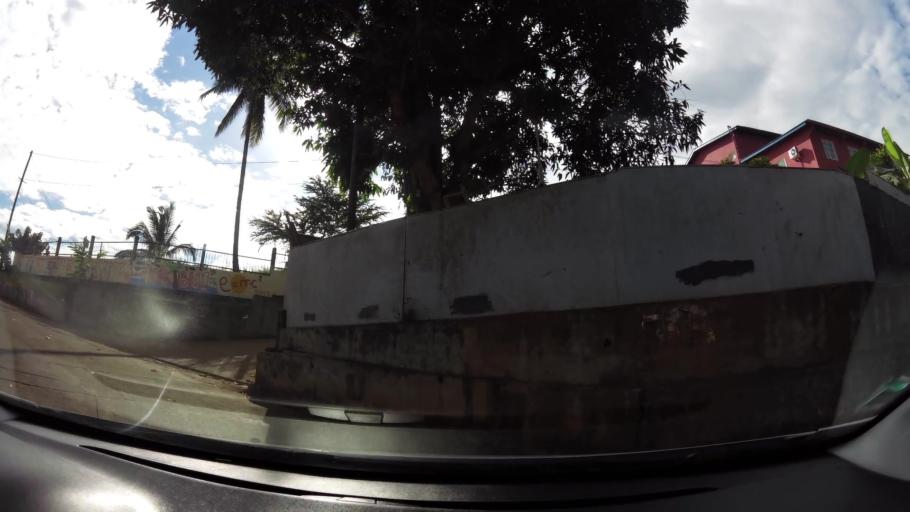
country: YT
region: Ouangani
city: Ouangani
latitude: -12.8409
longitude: 45.1307
